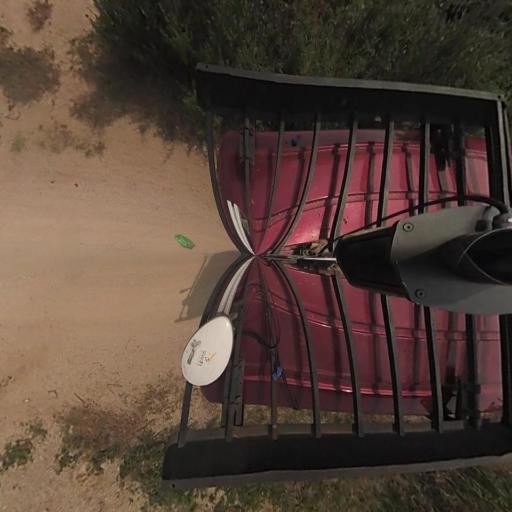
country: IN
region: Telangana
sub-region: Nalgonda
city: Nalgonda
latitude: 17.1954
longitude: 79.1360
